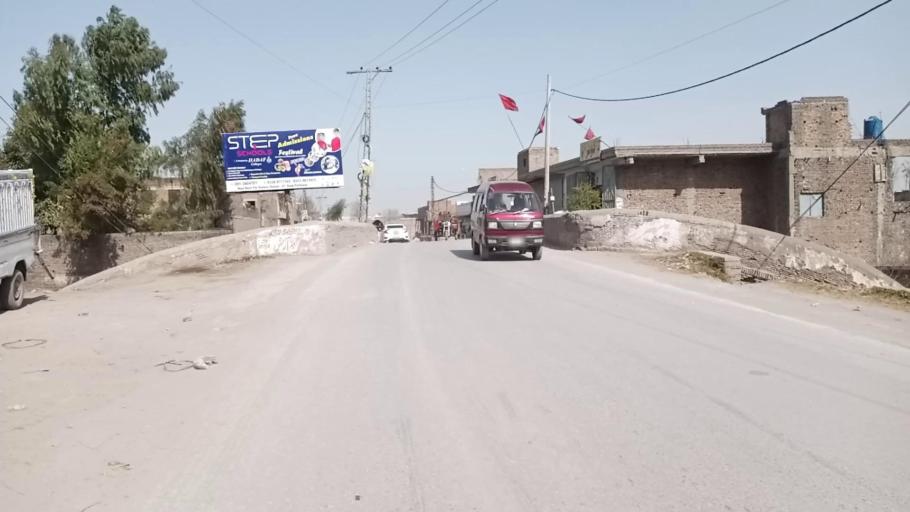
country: PK
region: Khyber Pakhtunkhwa
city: Peshawar
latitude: 34.0154
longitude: 71.6467
